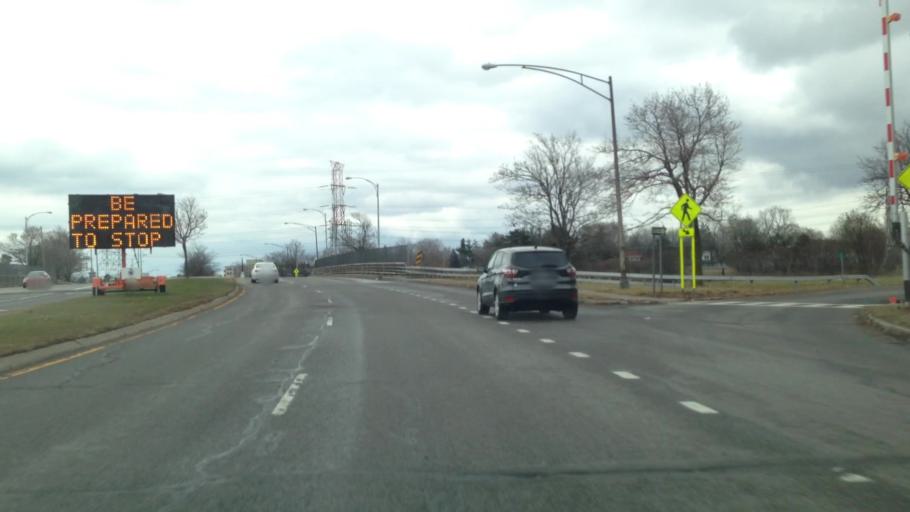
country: US
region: New York
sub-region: Erie County
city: Williamsville
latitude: 42.9589
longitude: -78.7679
